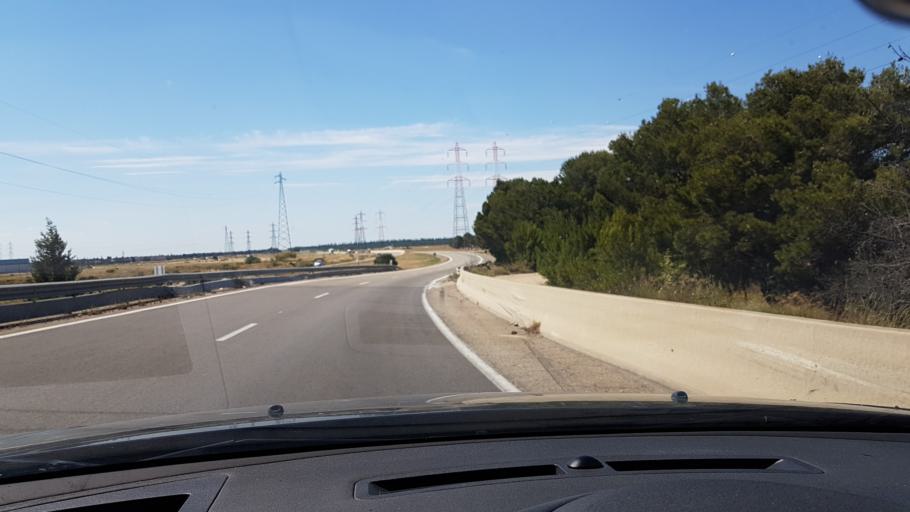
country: FR
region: Provence-Alpes-Cote d'Azur
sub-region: Departement des Bouches-du-Rhone
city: Fos-sur-Mer
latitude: 43.4797
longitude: 4.8945
